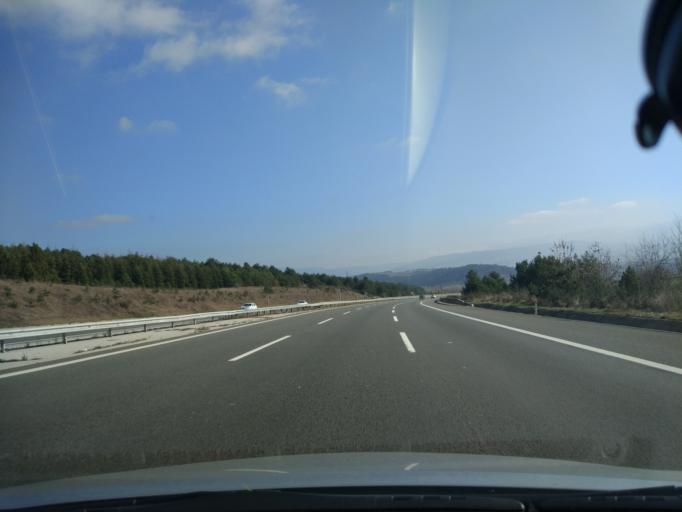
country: TR
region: Bolu
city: Bolu
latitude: 40.7803
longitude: 31.7153
